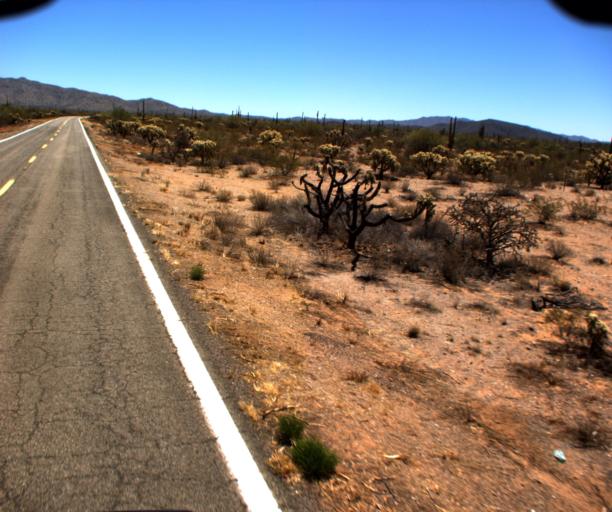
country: US
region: Arizona
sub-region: Pima County
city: Sells
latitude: 32.1820
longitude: -112.3105
